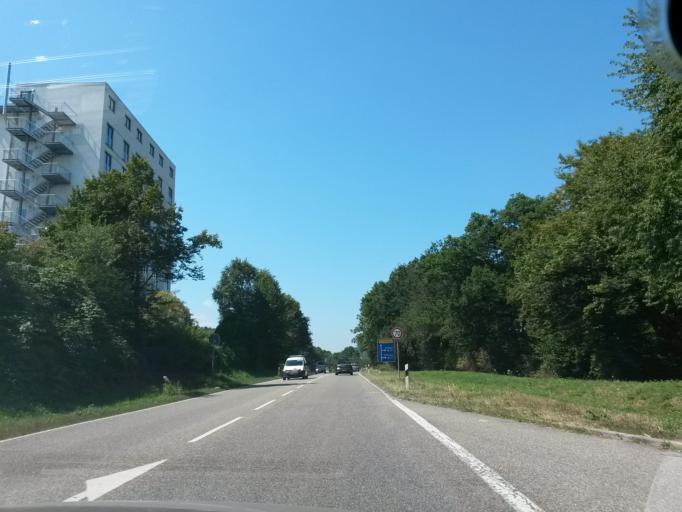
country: DE
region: Baden-Wuerttemberg
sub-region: Karlsruhe Region
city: Niefern-Oschelbronn
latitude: 48.9156
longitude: 8.7719
